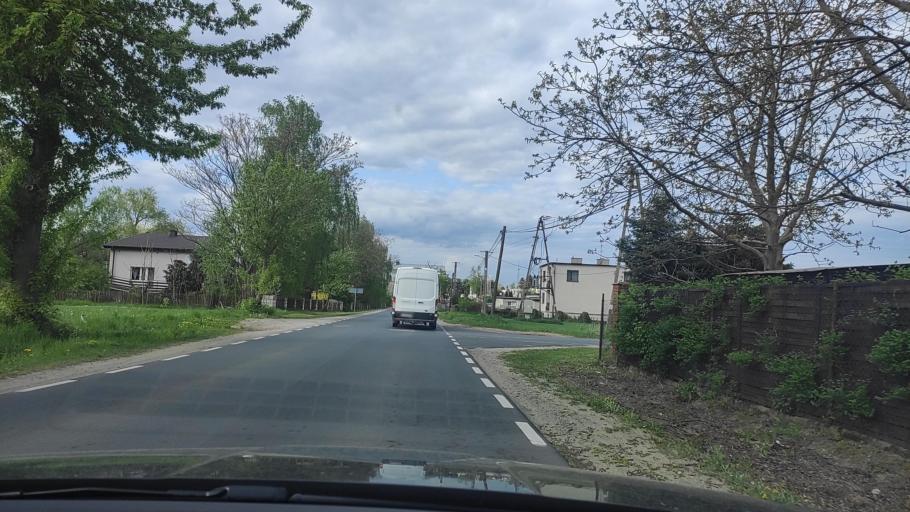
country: PL
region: Greater Poland Voivodeship
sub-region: Powiat poznanski
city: Kostrzyn
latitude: 52.4601
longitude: 17.1675
